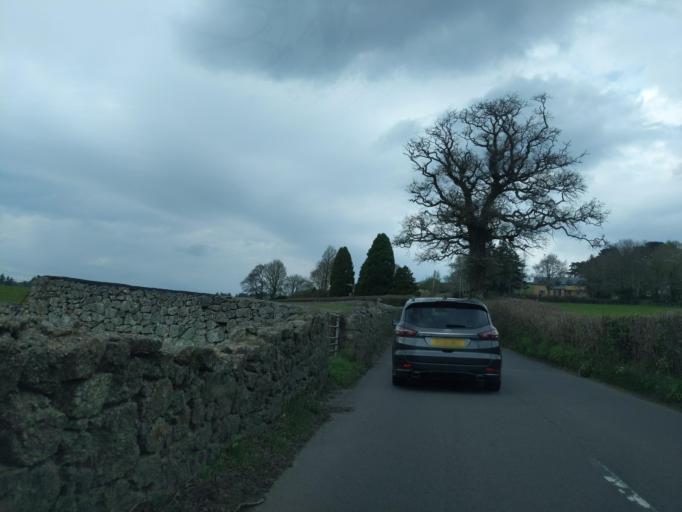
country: GB
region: England
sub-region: Devon
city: Bovey Tracey
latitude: 50.6922
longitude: -3.8246
